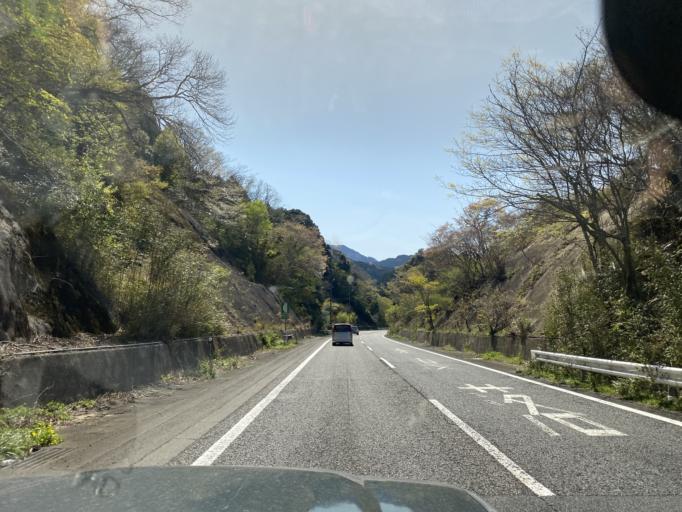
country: JP
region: Mie
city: Kameyama
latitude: 34.8369
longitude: 136.3401
